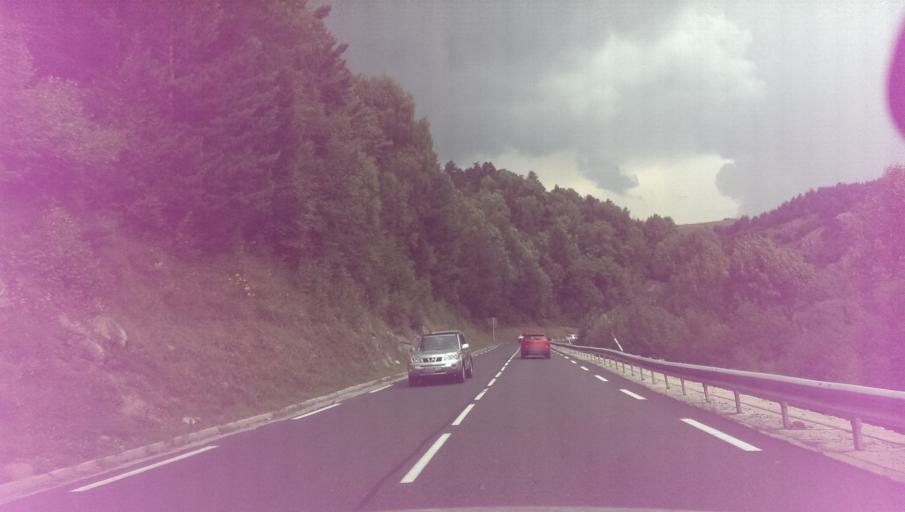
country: ES
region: Catalonia
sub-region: Provincia de Girona
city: Llivia
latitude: 42.5095
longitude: 2.1243
